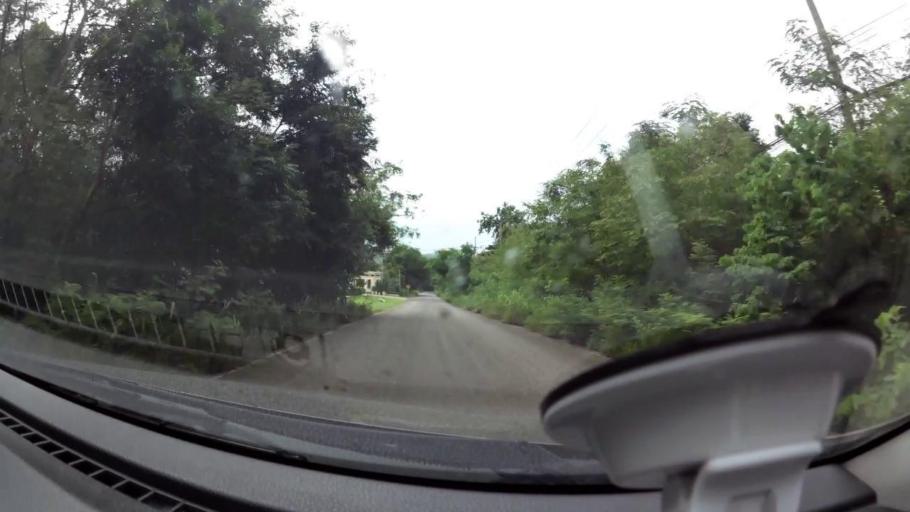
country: TH
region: Prachuap Khiri Khan
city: Pran Buri
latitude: 12.4398
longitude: 99.9706
